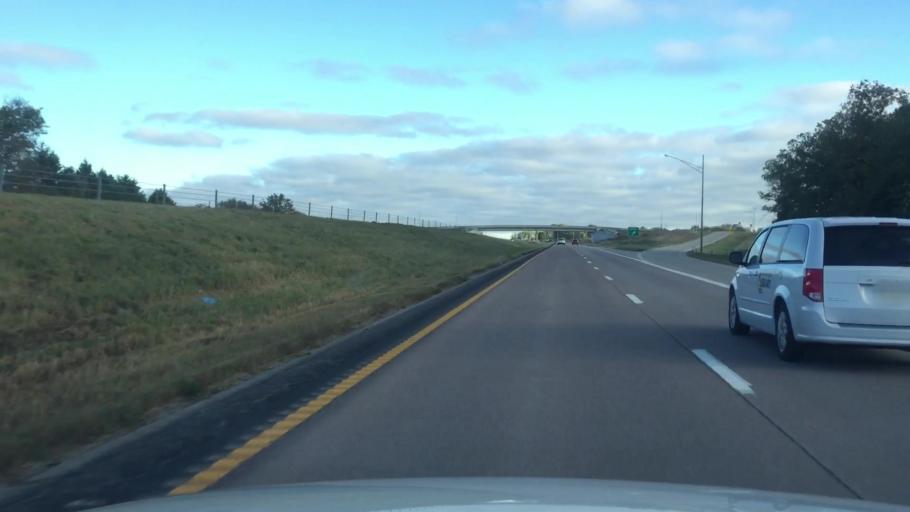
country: US
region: Missouri
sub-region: Boone County
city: Ashland
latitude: 38.8286
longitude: -92.2499
